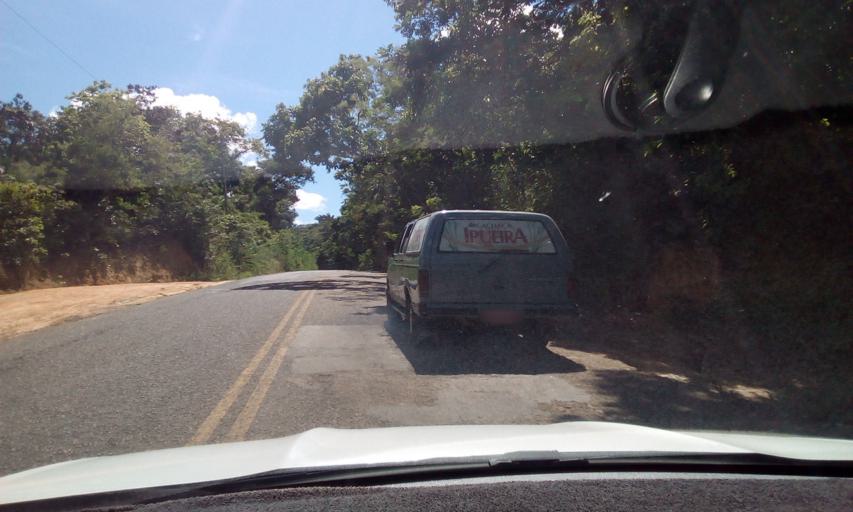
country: BR
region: Paraiba
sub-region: Areia
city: Areia
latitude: -6.9782
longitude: -35.7269
